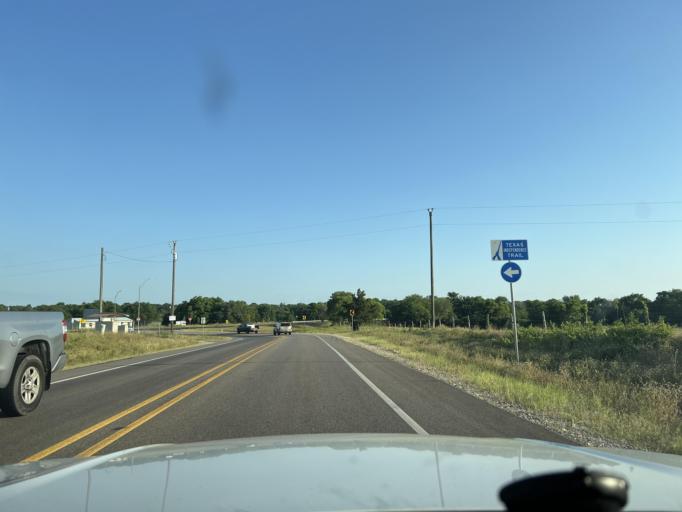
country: US
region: Texas
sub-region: Washington County
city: Brenham
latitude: 30.1988
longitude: -96.3645
